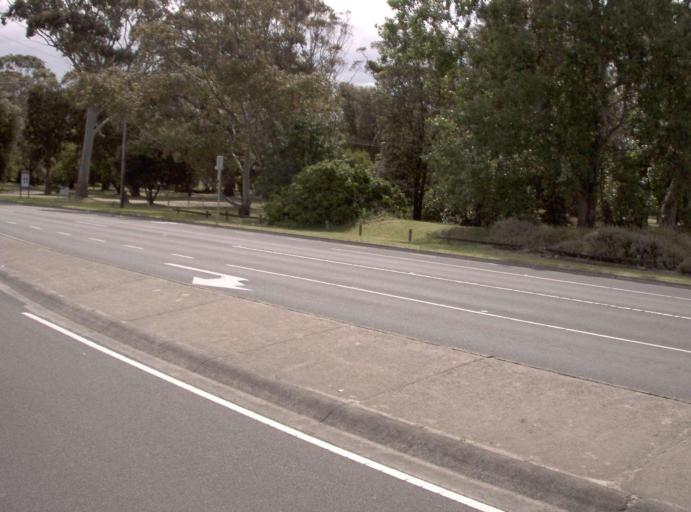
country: AU
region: Victoria
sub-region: Mornington Peninsula
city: Rosebud West
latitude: -38.3601
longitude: 144.8894
